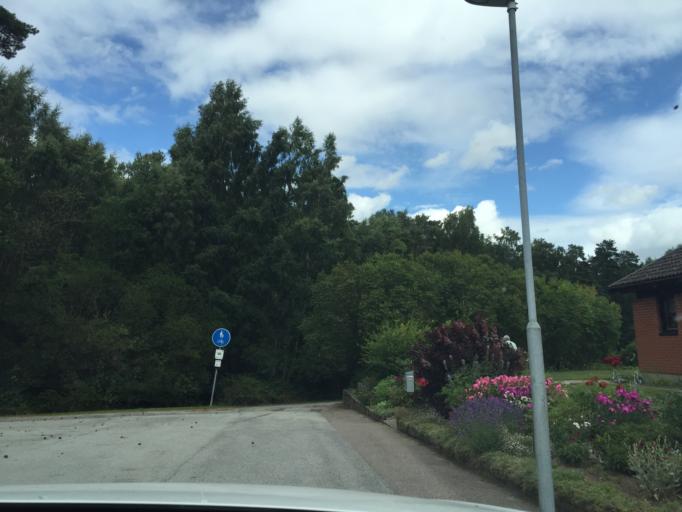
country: SE
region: Skane
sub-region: Sjobo Kommun
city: Blentarp
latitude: 55.5831
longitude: 13.5944
